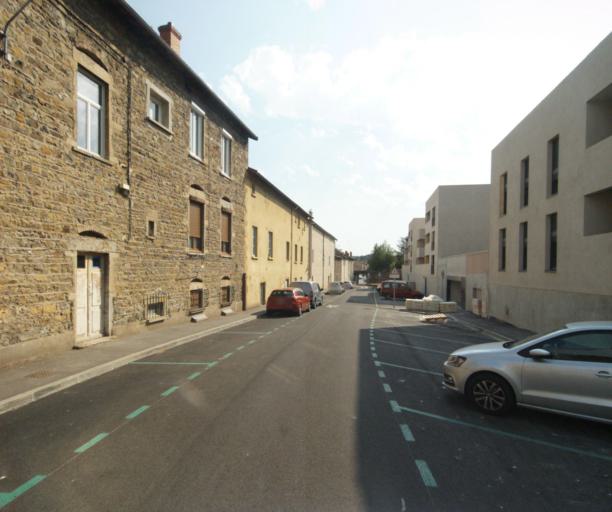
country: FR
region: Rhone-Alpes
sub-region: Departement du Rhone
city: Saint-Germain-Nuelles
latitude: 45.8341
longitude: 4.6145
